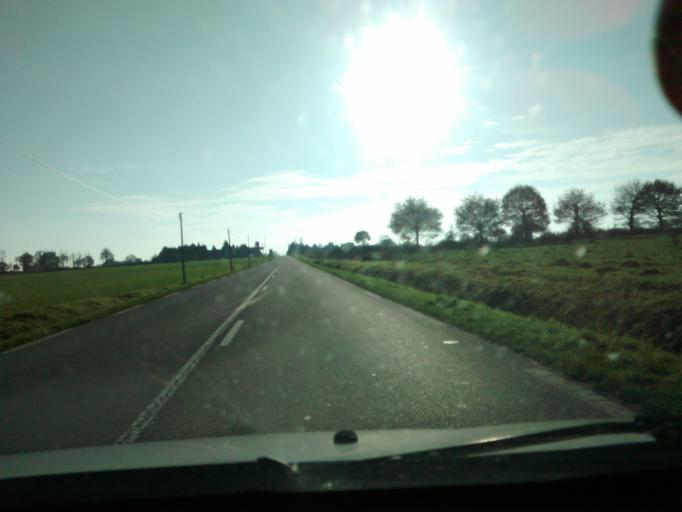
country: FR
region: Brittany
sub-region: Departement d'Ille-et-Vilaine
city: Tremblay
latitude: 48.3846
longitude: -1.4918
